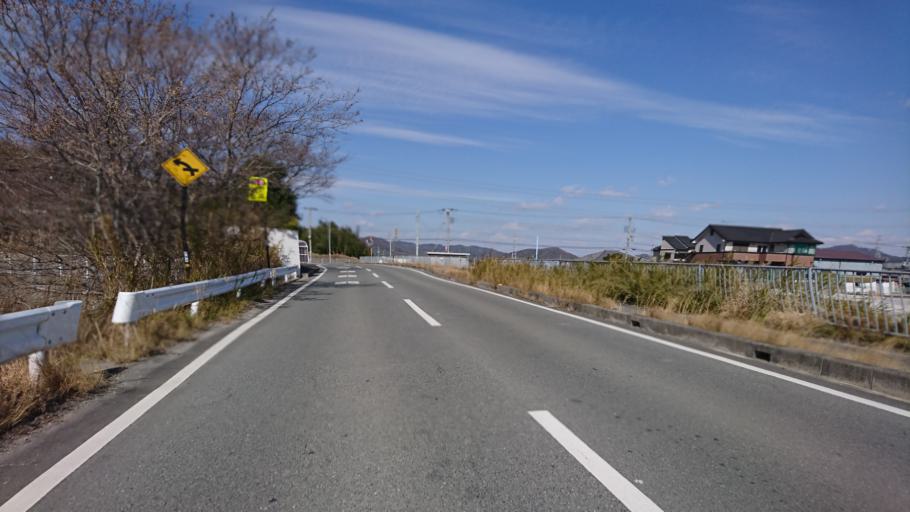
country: JP
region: Hyogo
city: Kakogawacho-honmachi
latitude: 34.7985
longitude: 134.8114
